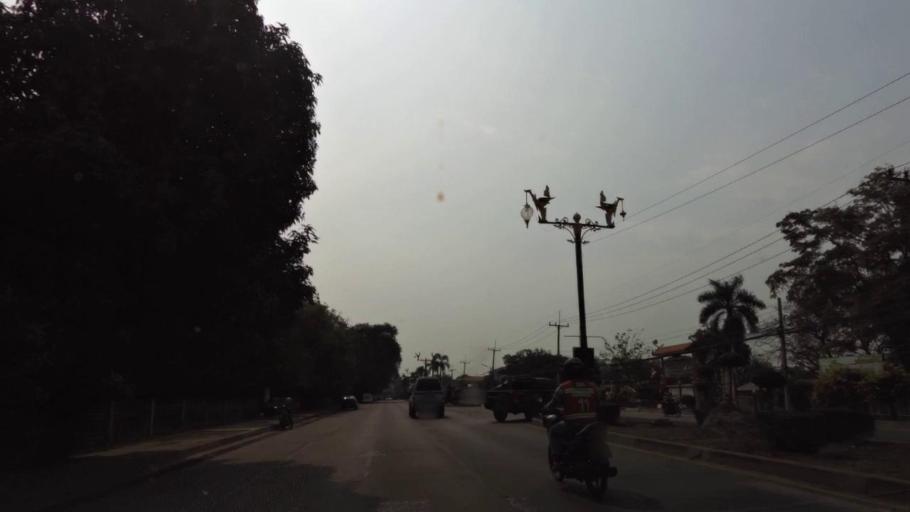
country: TH
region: Phra Nakhon Si Ayutthaya
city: Phra Nakhon Si Ayutthaya
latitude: 14.3499
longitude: 100.5651
